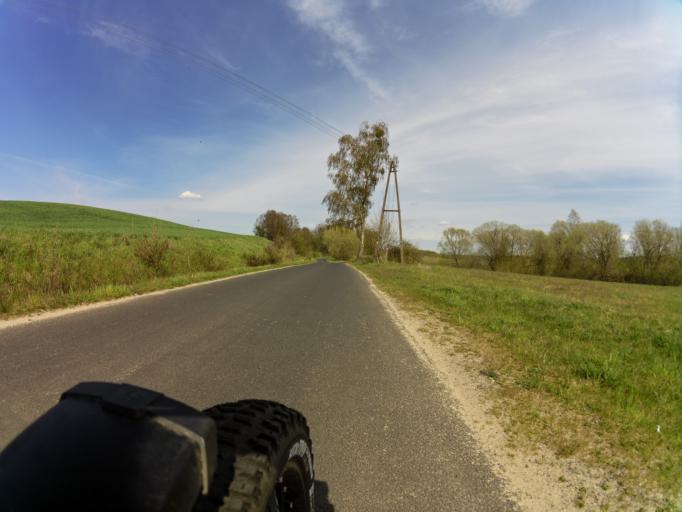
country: PL
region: West Pomeranian Voivodeship
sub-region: Powiat lobeski
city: Resko
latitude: 53.7853
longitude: 15.4236
